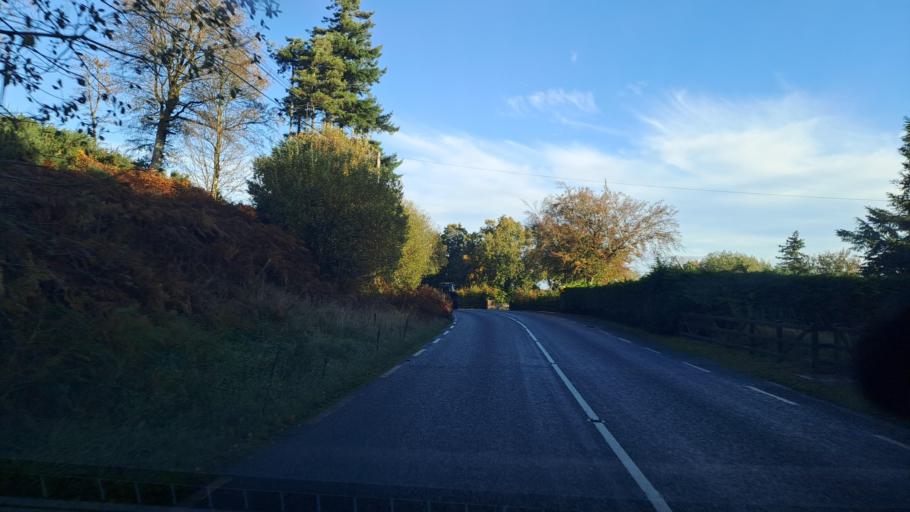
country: IE
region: Ulster
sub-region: County Monaghan
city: Monaghan
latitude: 54.2136
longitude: -6.9844
